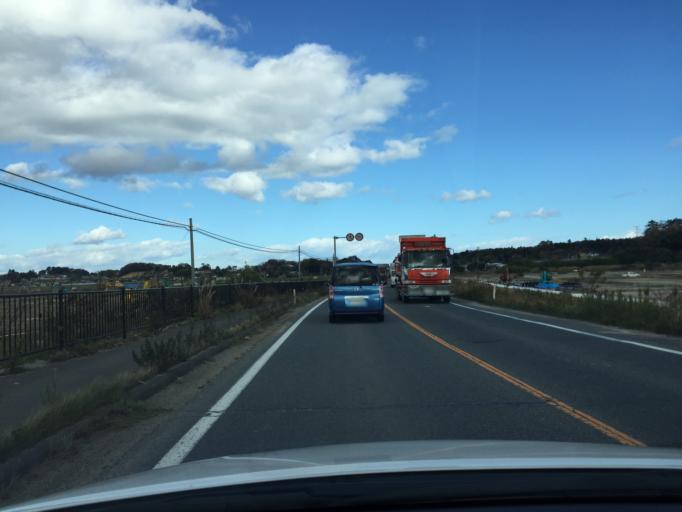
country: JP
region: Fukushima
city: Namie
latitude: 37.5984
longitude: 141.0035
